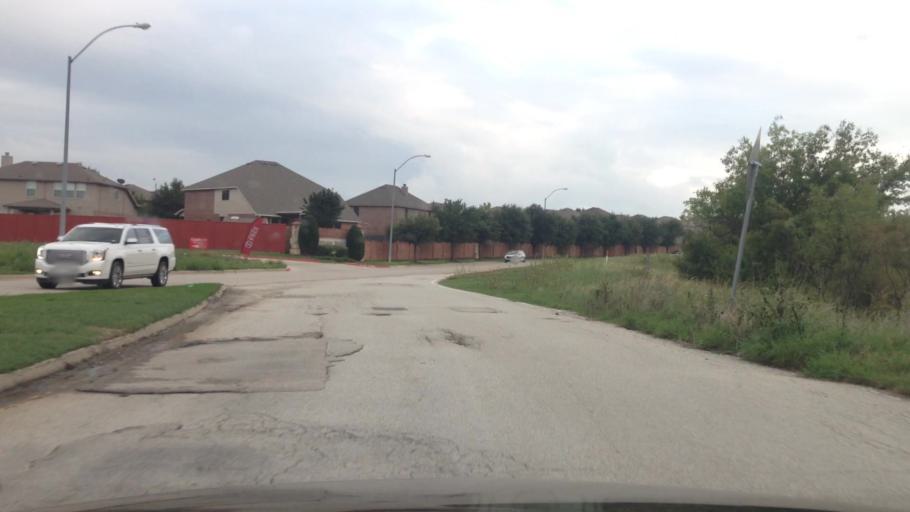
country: US
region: Texas
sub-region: Tarrant County
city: Crowley
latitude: 32.5771
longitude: -97.3288
